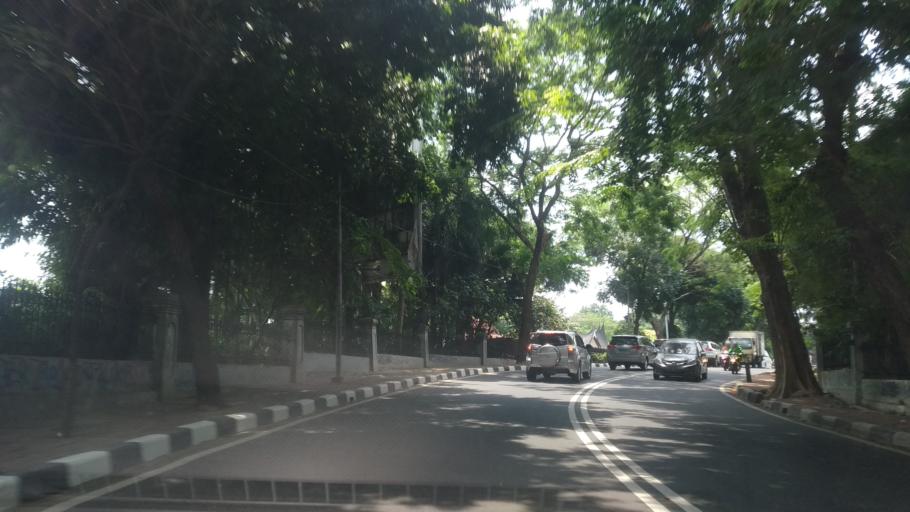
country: ID
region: Banten
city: South Tangerang
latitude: -6.2531
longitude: 106.7698
